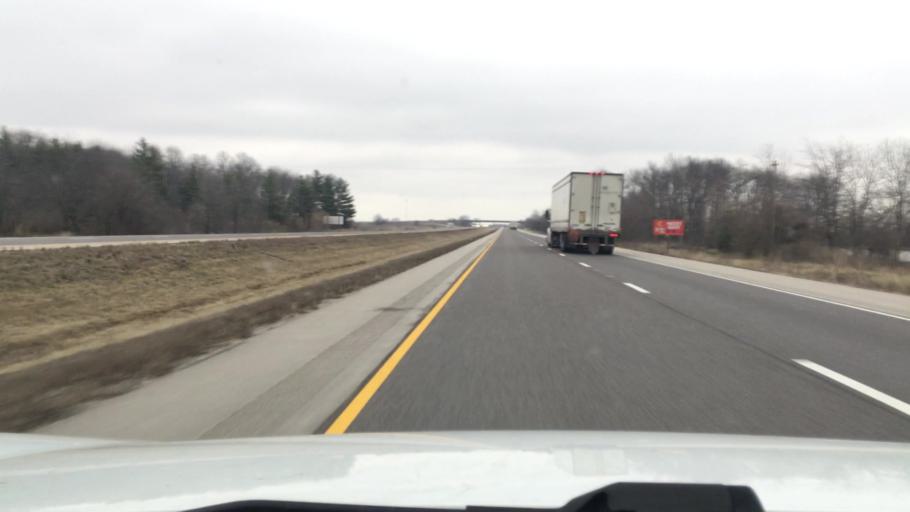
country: US
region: Illinois
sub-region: Fayette County
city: Saint Elmo
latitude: 39.0176
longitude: -88.8350
